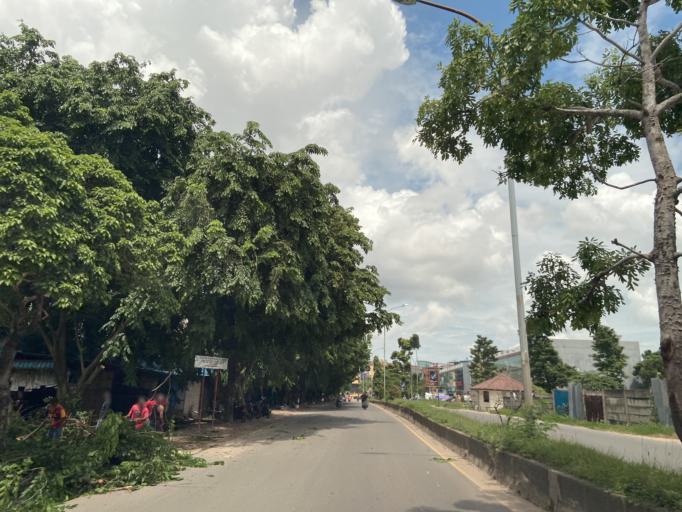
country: SG
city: Singapore
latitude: 1.1447
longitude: 104.0034
